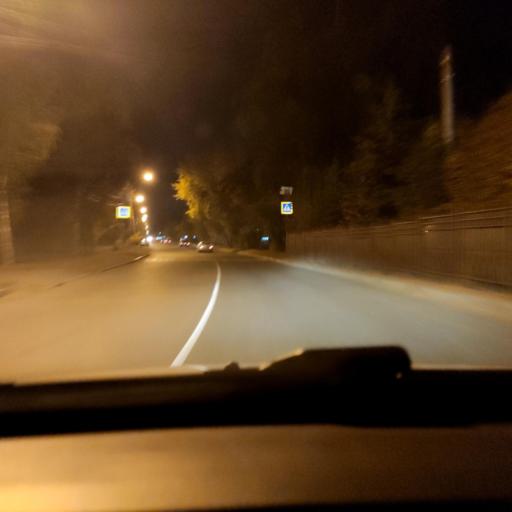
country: RU
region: Voronezj
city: Voronezh
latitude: 51.6559
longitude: 39.2123
